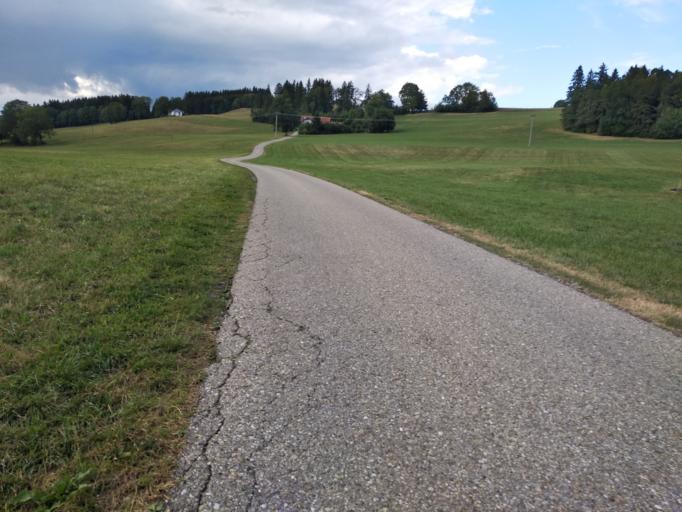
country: DE
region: Bavaria
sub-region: Swabia
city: Haldenwang
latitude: 47.8212
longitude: 10.3309
